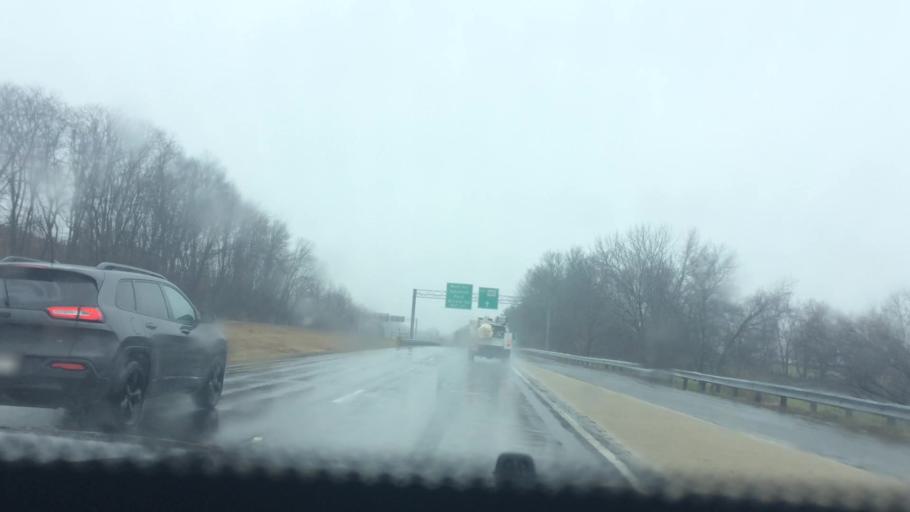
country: US
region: Massachusetts
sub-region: Essex County
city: Haverhill
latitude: 42.7551
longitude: -71.1138
